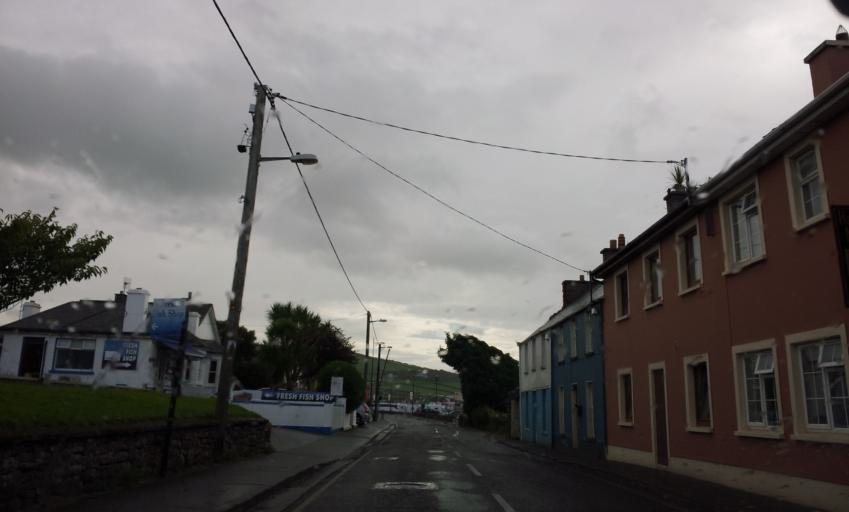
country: IE
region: Munster
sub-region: Ciarrai
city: Dingle
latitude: 52.1397
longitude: -10.2801
